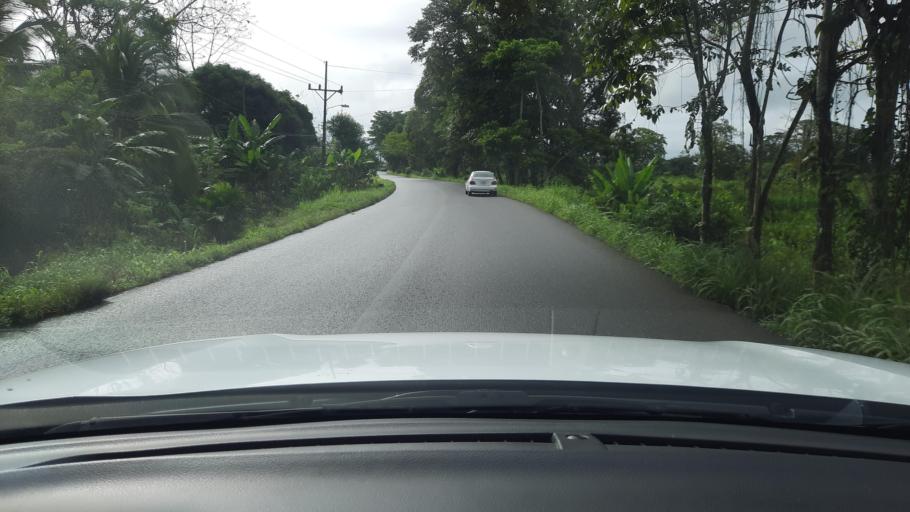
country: CR
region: Alajuela
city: San Jose
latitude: 10.9353
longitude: -85.1065
